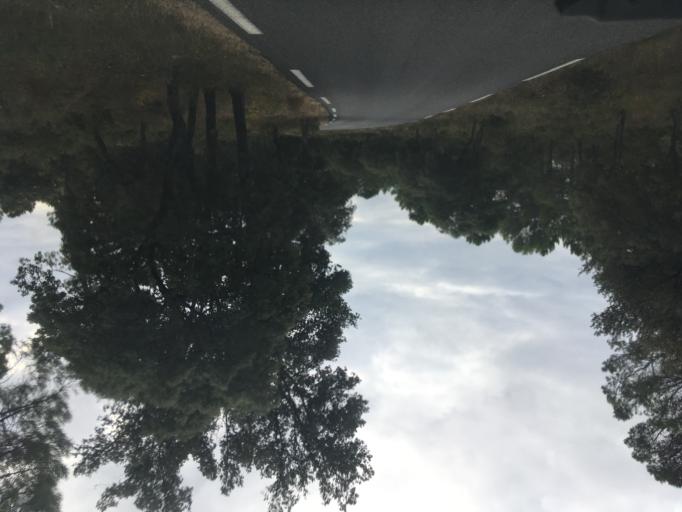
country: FR
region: Provence-Alpes-Cote d'Azur
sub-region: Departement du Var
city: Villecroze
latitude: 43.5540
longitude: 6.3287
